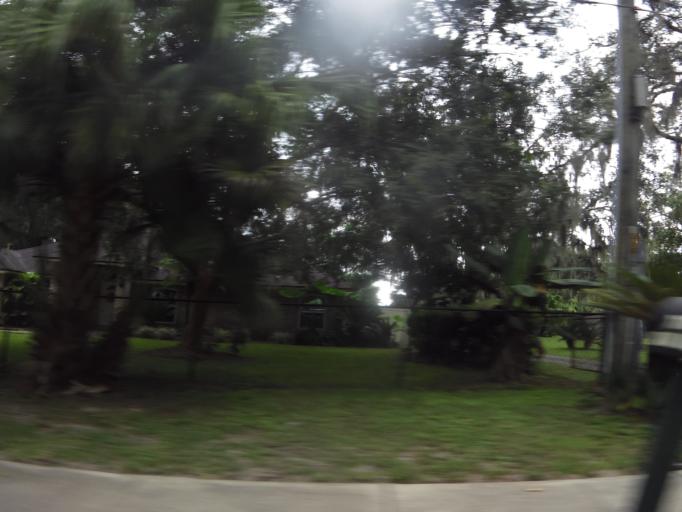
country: US
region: Florida
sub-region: Clay County
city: Bellair-Meadowbrook Terrace
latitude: 30.2454
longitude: -81.7137
